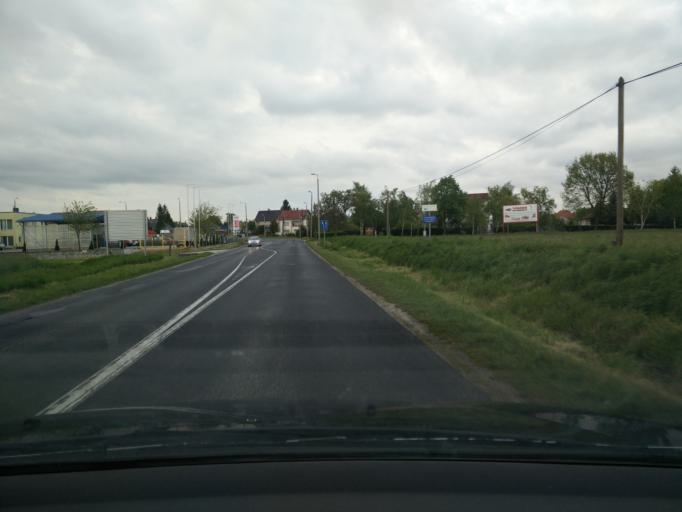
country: HU
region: Gyor-Moson-Sopron
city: Tet
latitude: 47.5108
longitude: 17.5147
